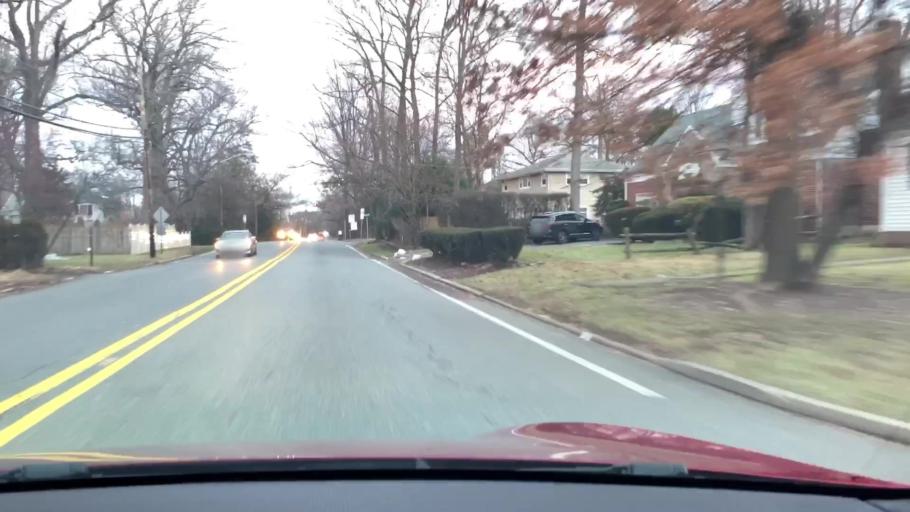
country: US
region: New Jersey
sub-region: Bergen County
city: Tenafly
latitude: 40.9339
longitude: -73.9774
